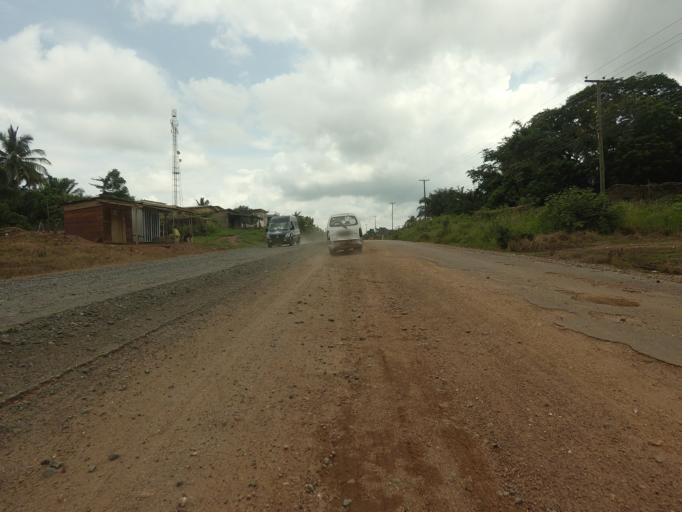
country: GH
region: Volta
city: Ho
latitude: 6.6252
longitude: 0.3105
